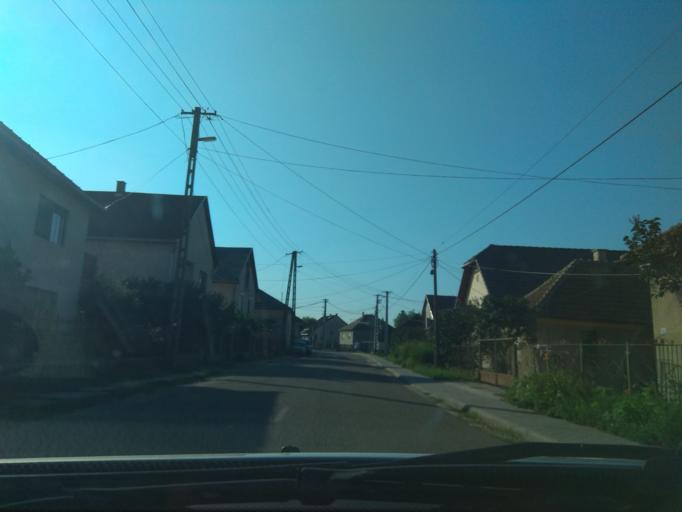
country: HU
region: Borsod-Abauj-Zemplen
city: Harsany
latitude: 47.9859
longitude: 20.7802
